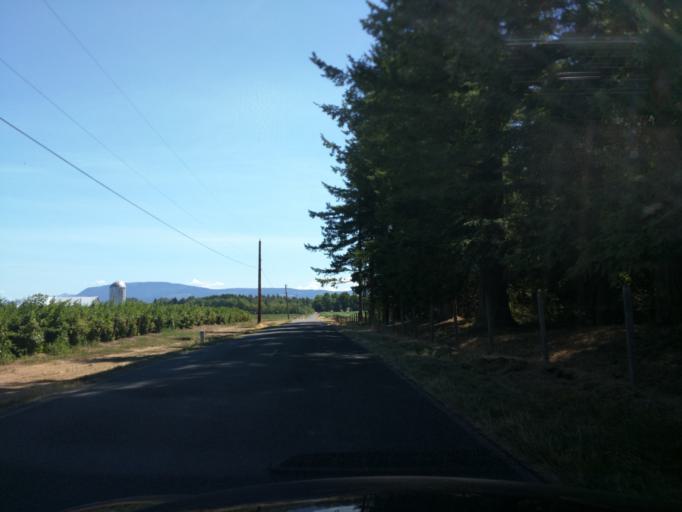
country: US
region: Washington
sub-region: Whatcom County
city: Lynden
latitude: 48.8698
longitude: -122.4292
